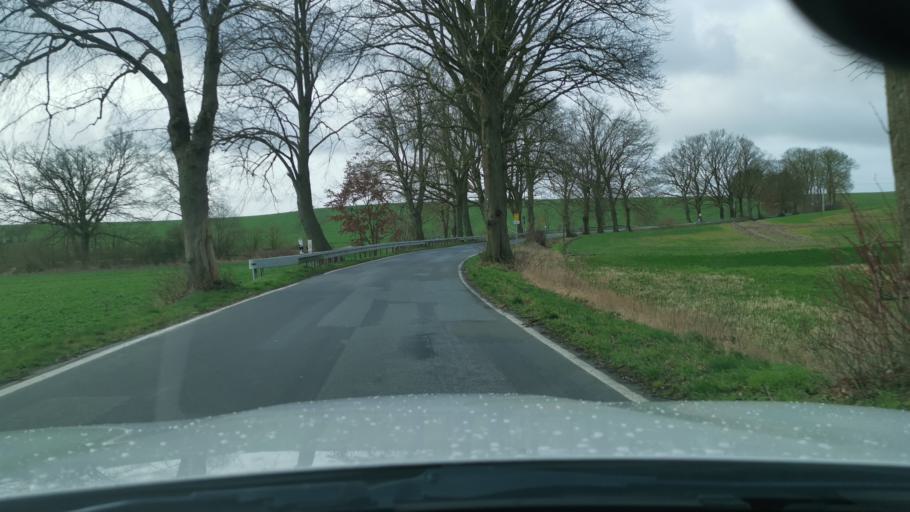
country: DE
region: Mecklenburg-Vorpommern
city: Tessin
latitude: 54.0144
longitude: 12.4205
